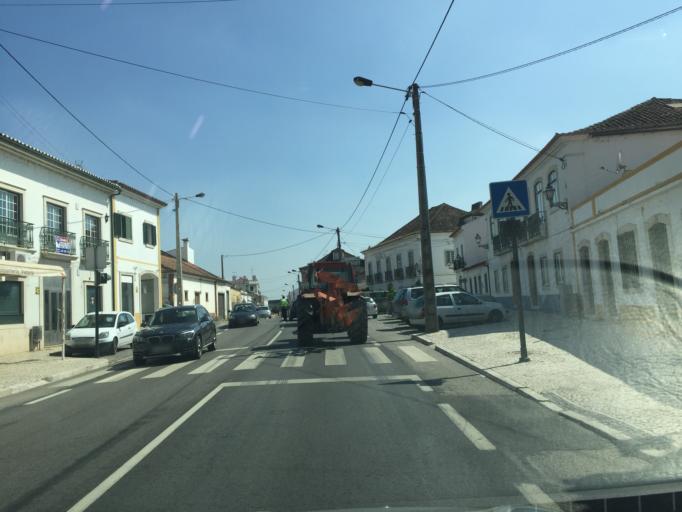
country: PT
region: Santarem
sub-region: Golega
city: Golega
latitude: 39.3549
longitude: -8.4838
